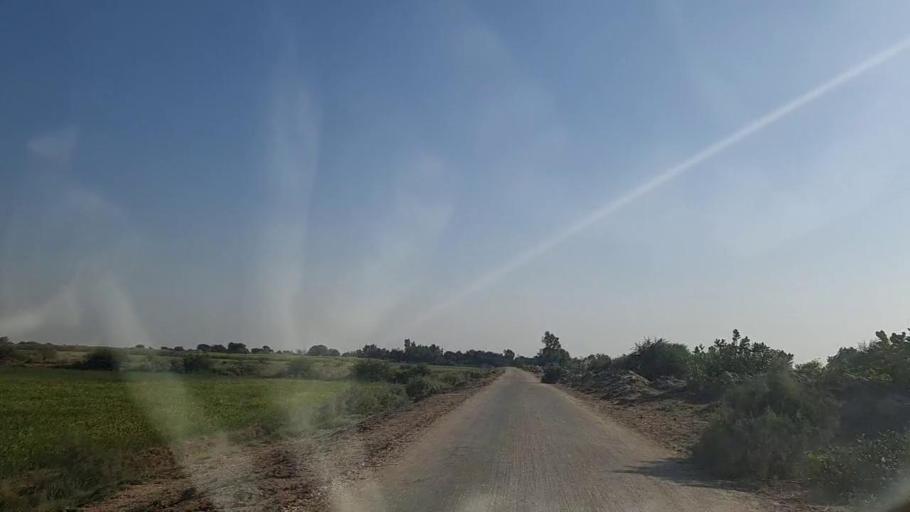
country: PK
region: Sindh
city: Mirpur Batoro
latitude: 24.5565
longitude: 68.1716
